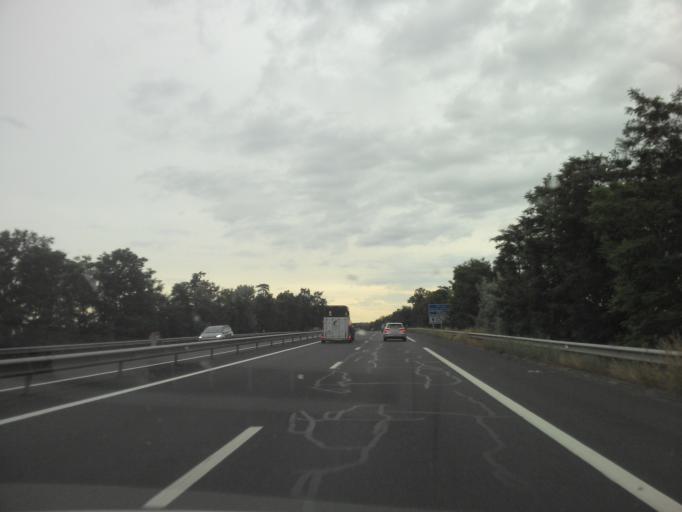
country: FR
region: Auvergne
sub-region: Departement du Puy-de-Dome
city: Riom
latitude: 45.9011
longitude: 3.1544
